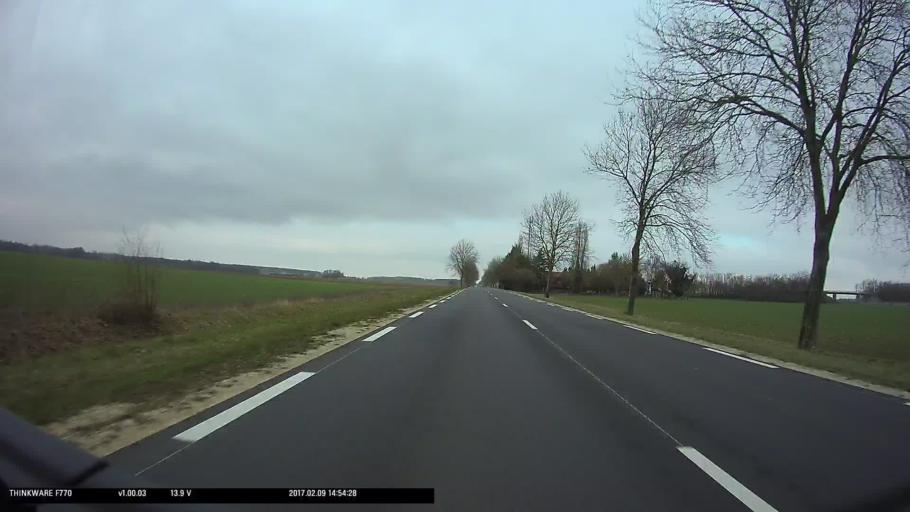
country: FR
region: Centre
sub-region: Departement du Cher
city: Levet
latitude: 46.8925
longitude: 2.4148
